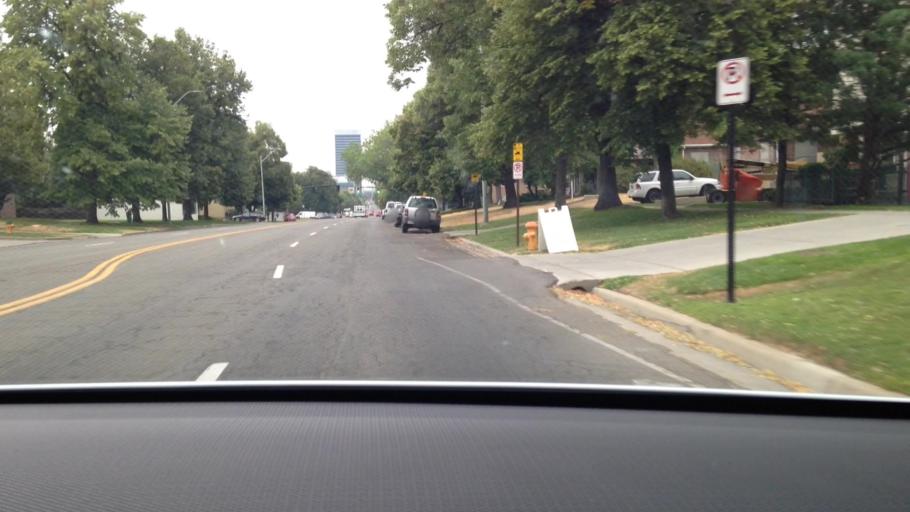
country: US
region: Utah
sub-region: Salt Lake County
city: Salt Lake City
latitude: 40.7673
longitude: -111.8715
